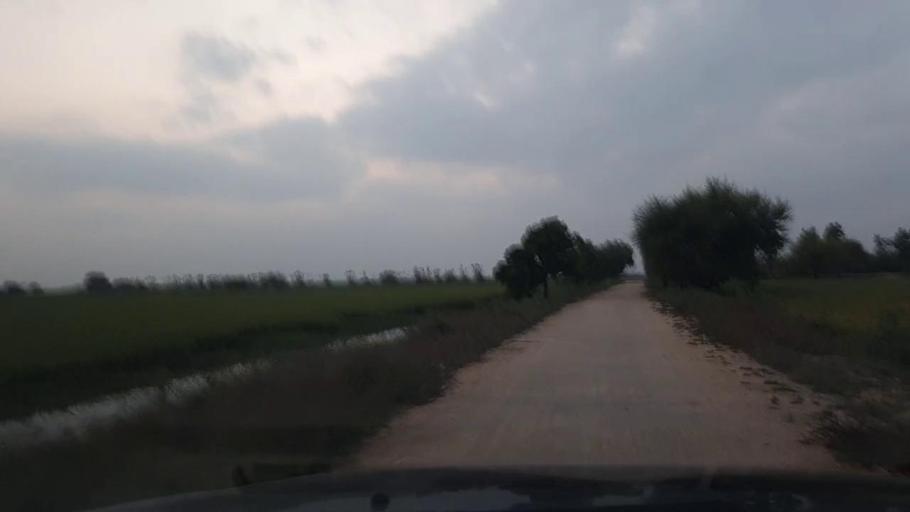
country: PK
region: Sindh
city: Jati
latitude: 24.5195
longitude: 68.3691
